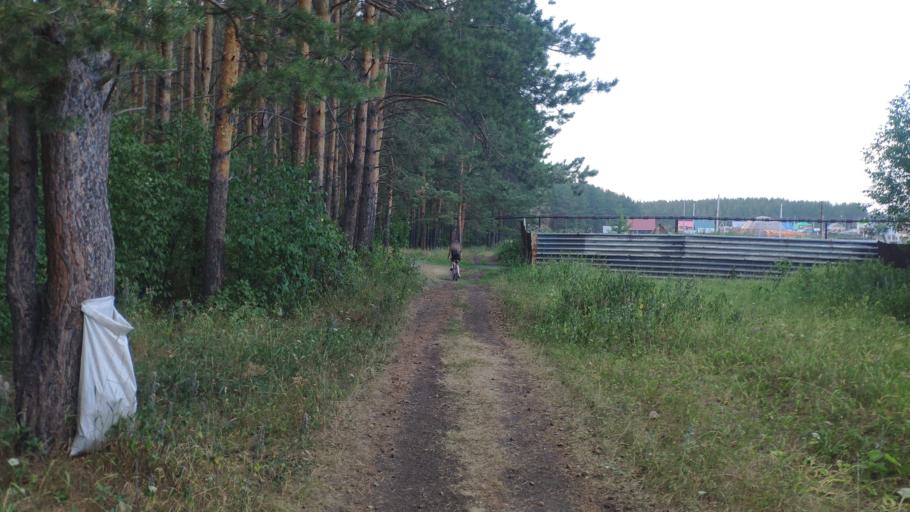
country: RU
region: Bashkortostan
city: Abzakovo
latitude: 53.8069
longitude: 58.6421
